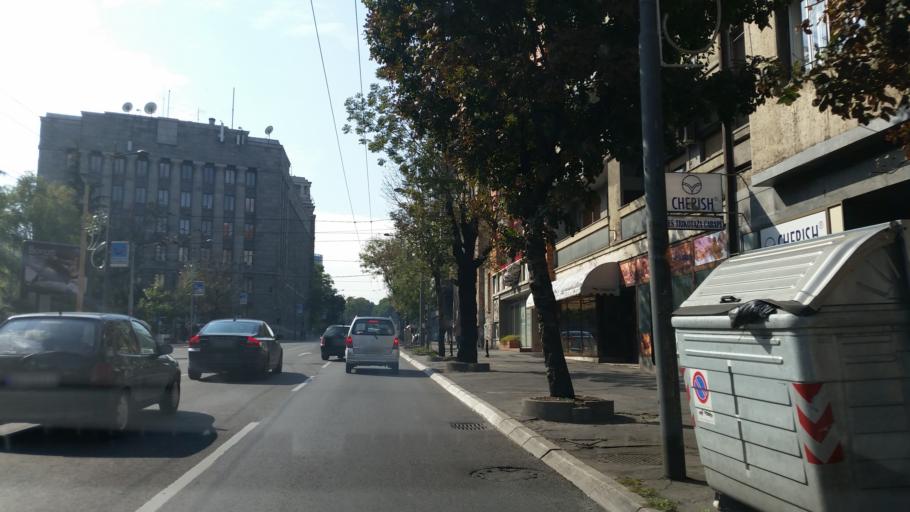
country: RS
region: Central Serbia
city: Belgrade
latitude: 44.8117
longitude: 20.4690
